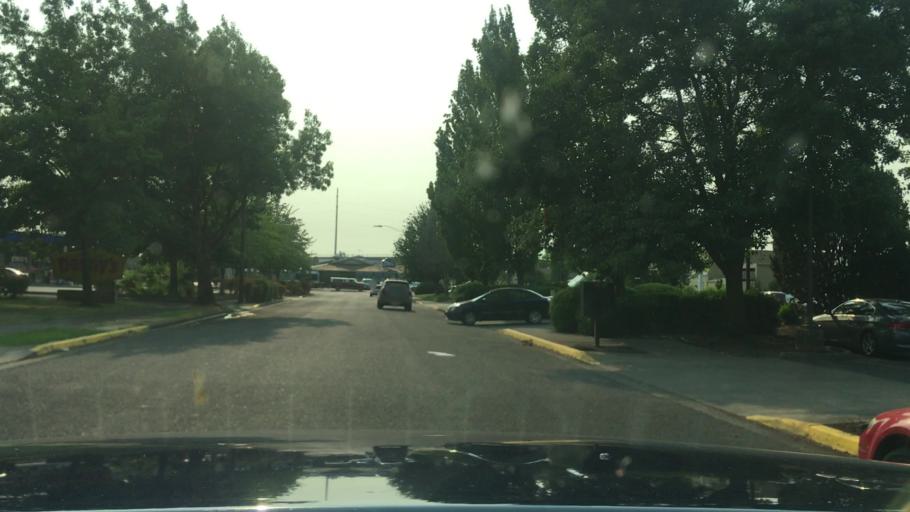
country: US
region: Oregon
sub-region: Lane County
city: Springfield
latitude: 44.0826
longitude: -123.0398
